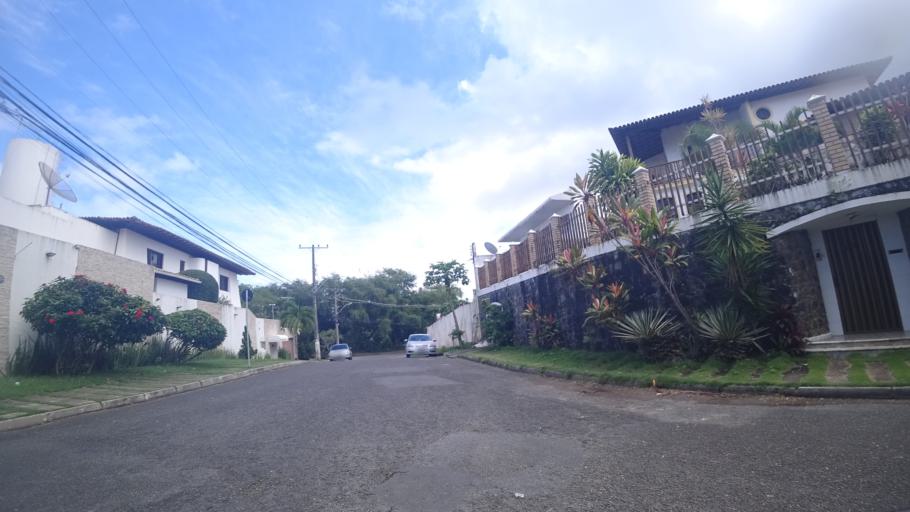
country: BR
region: Bahia
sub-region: Salvador
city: Salvador
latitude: -12.9910
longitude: -38.4643
